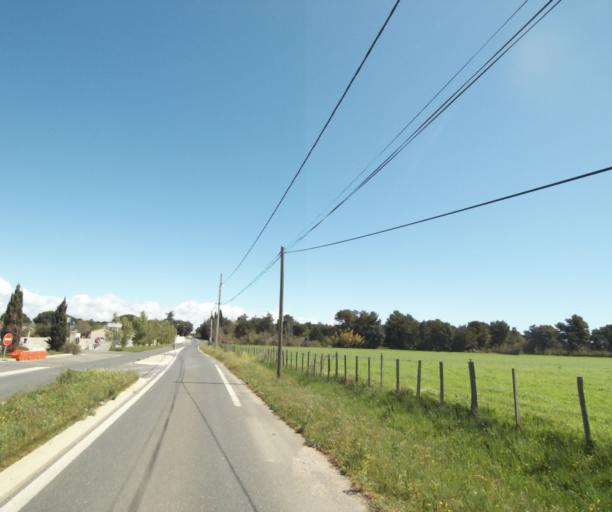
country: FR
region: Languedoc-Roussillon
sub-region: Departement de l'Herault
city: Perols
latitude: 43.5591
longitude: 3.9359
